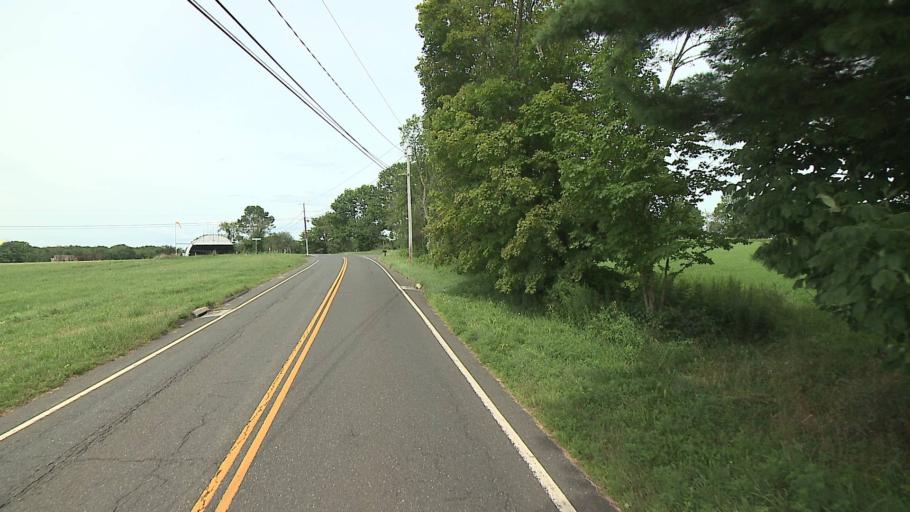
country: US
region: Connecticut
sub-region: Litchfield County
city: Woodbury
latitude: 41.5571
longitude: -73.2601
